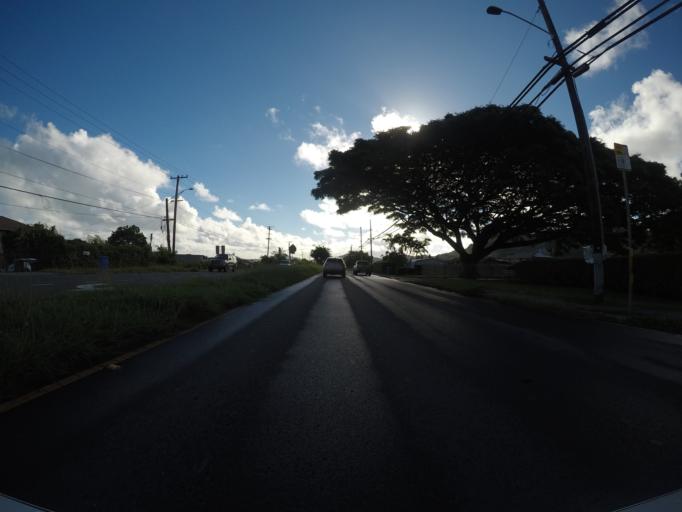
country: US
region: Hawaii
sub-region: Honolulu County
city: Kane'ohe
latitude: 21.4034
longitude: -157.7975
